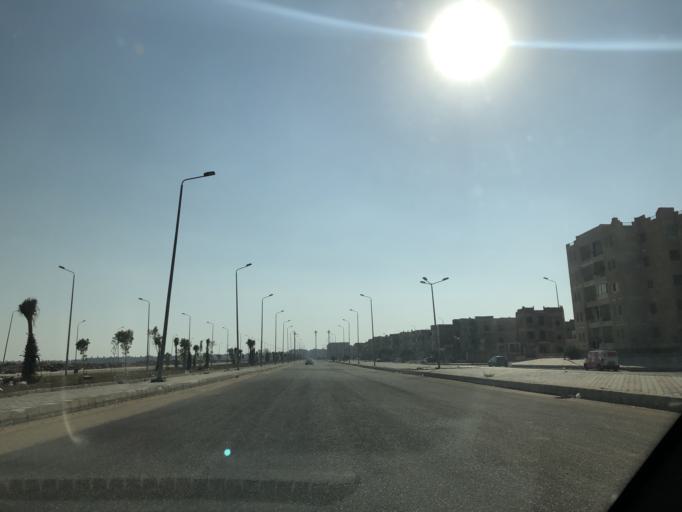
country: EG
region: Al Jizah
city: Madinat Sittah Uktubar
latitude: 29.9255
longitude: 31.0674
